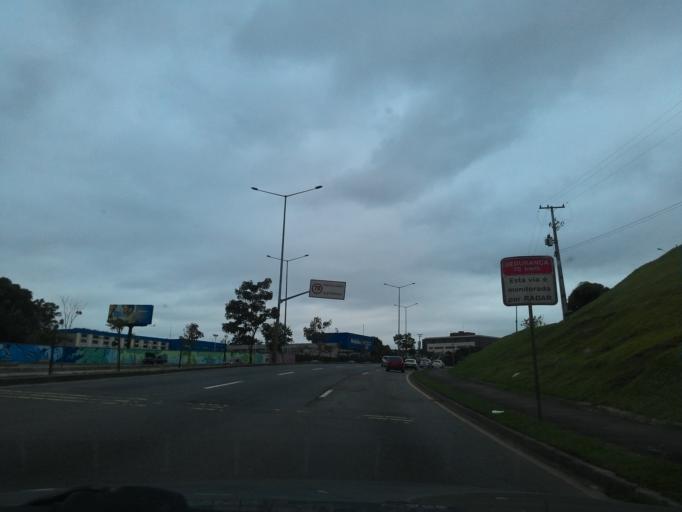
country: BR
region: Parana
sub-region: Curitiba
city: Curitiba
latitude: -25.4561
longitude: -49.2486
